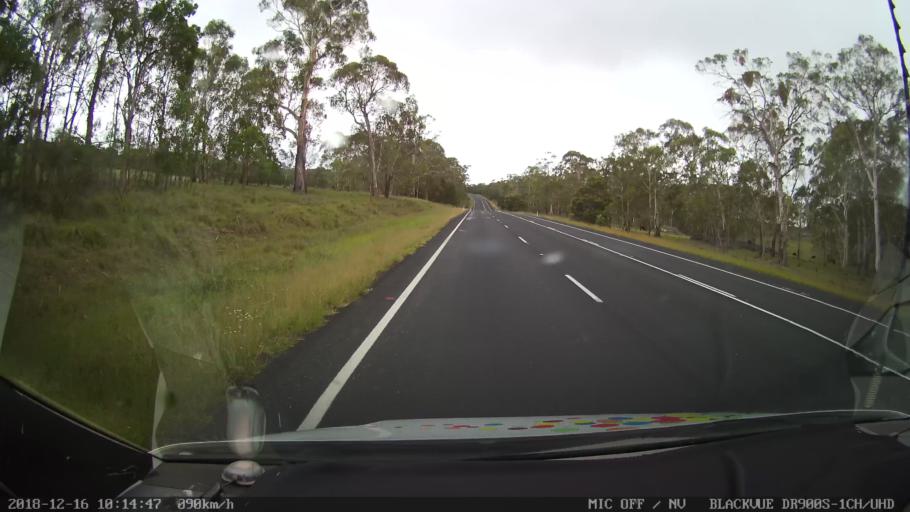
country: AU
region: New South Wales
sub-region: Tenterfield Municipality
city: Carrolls Creek
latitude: -29.2833
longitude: 151.9659
